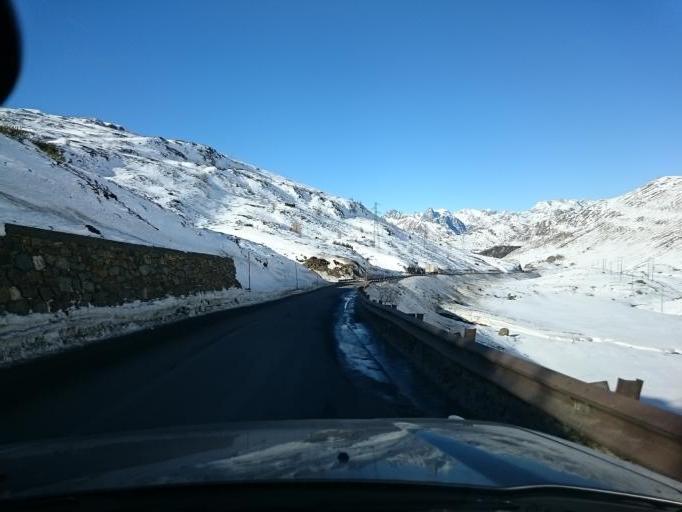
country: IT
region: Lombardy
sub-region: Provincia di Sondrio
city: Livigno
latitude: 46.5000
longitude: 10.2043
